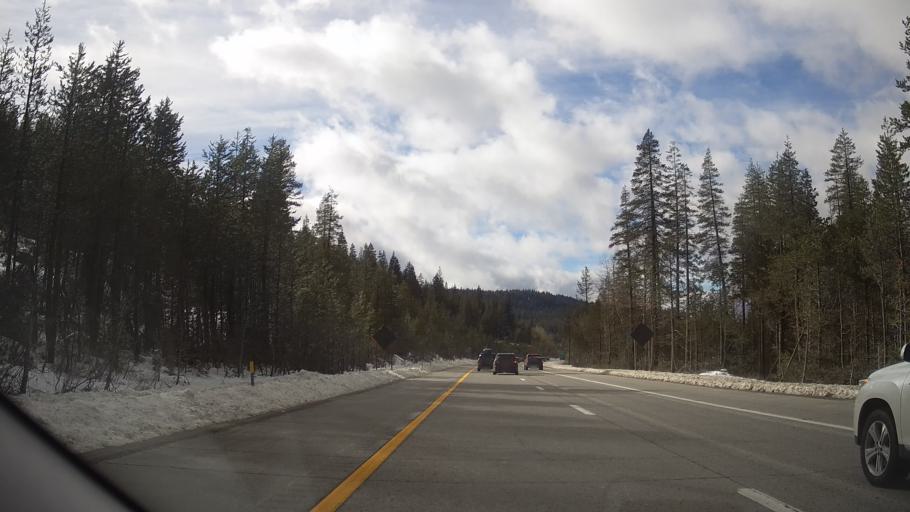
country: US
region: California
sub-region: Nevada County
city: Truckee
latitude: 39.3174
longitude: -120.4334
